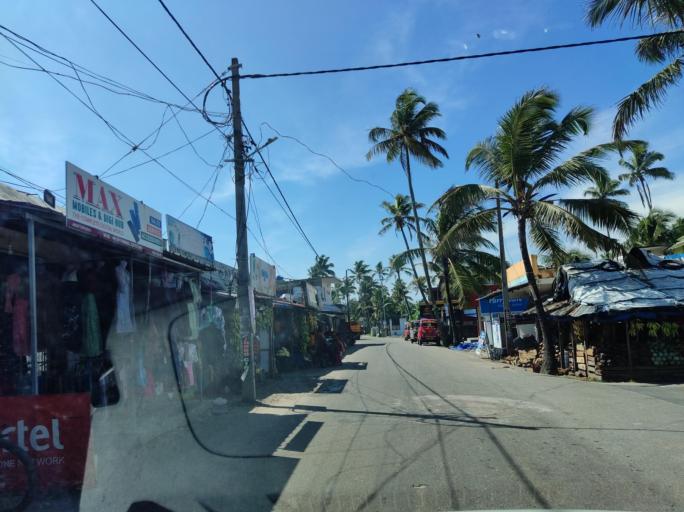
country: IN
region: Kerala
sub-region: Alappuzha
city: Kayankulam
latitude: 9.2161
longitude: 76.4270
